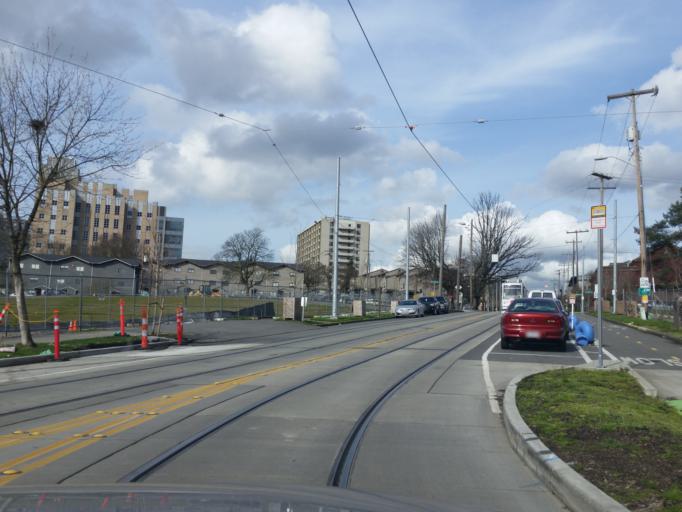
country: US
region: Washington
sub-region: King County
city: Seattle
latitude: 47.6019
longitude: -122.3207
